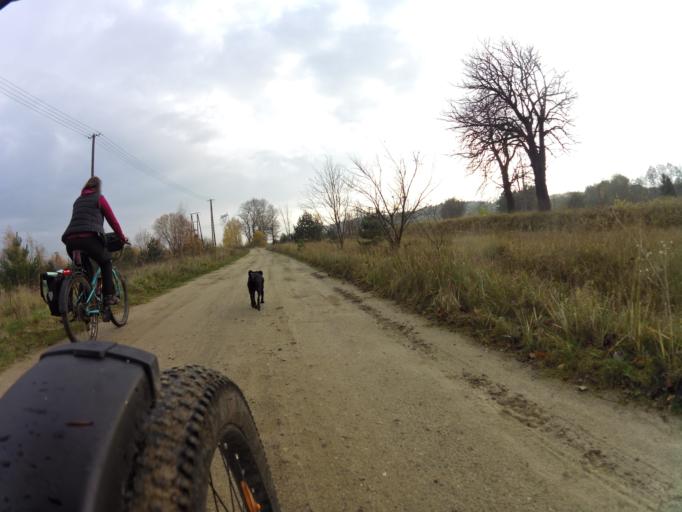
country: PL
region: Pomeranian Voivodeship
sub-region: Powiat wejherowski
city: Gniewino
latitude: 54.7102
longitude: 18.0982
